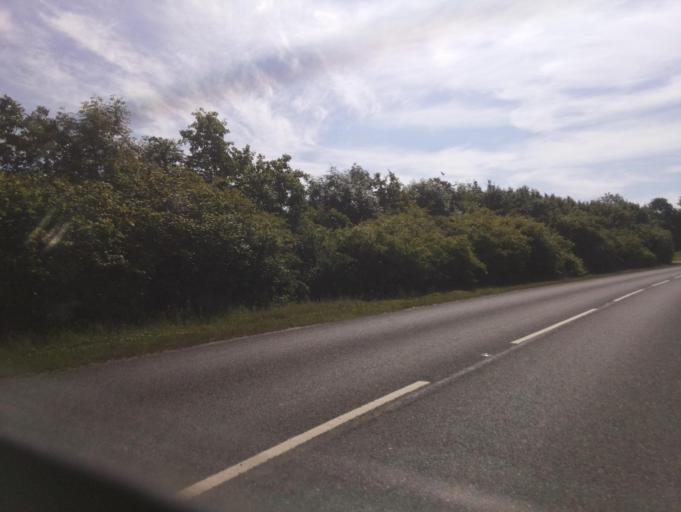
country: GB
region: England
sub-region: Lincolnshire
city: Skellingthorpe
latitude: 53.1657
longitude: -0.6398
